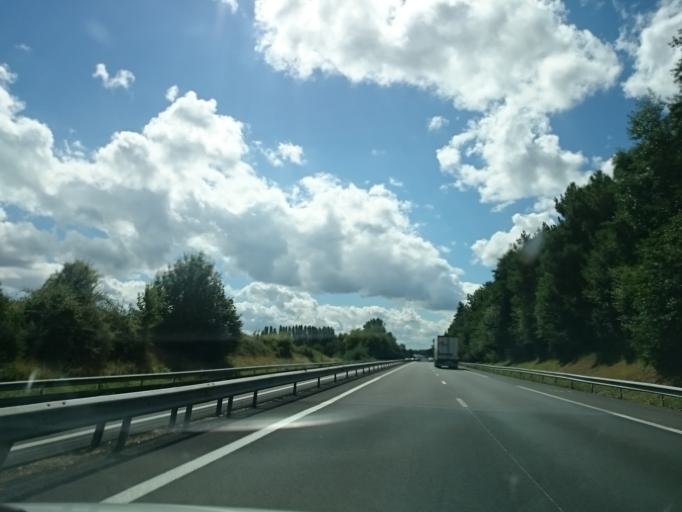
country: FR
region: Pays de la Loire
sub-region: Departement de Maine-et-Loire
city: Seiches-sur-le-Loir
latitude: 47.5944
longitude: -0.3167
